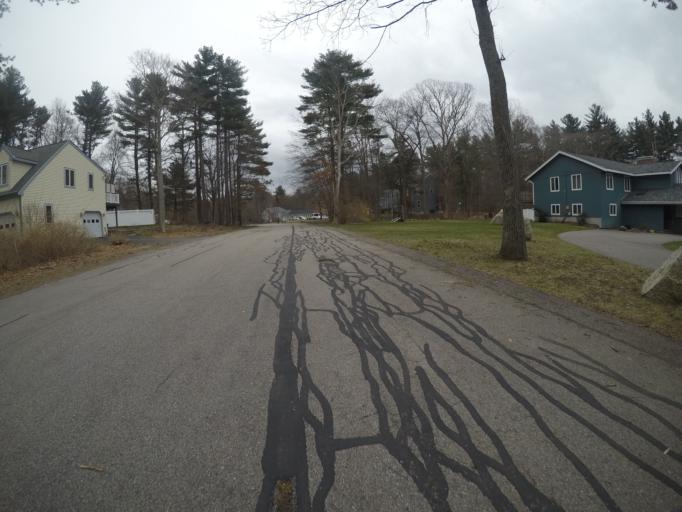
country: US
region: Massachusetts
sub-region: Bristol County
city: Easton
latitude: 42.0480
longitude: -71.1417
